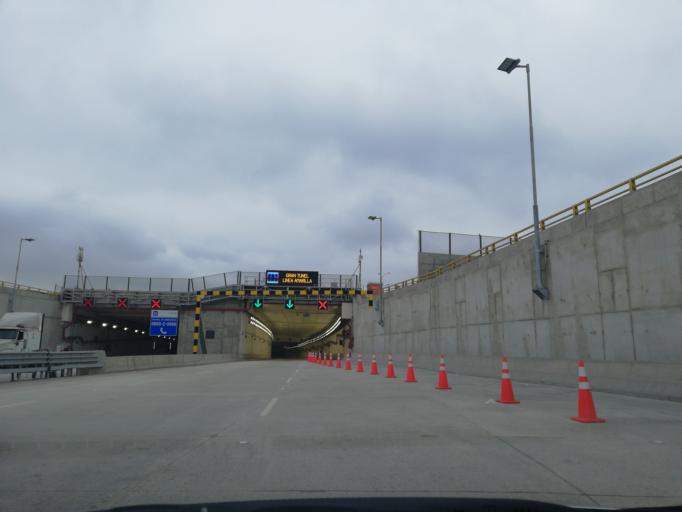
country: PE
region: Lima
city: Lima
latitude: -12.0433
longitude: -77.0209
